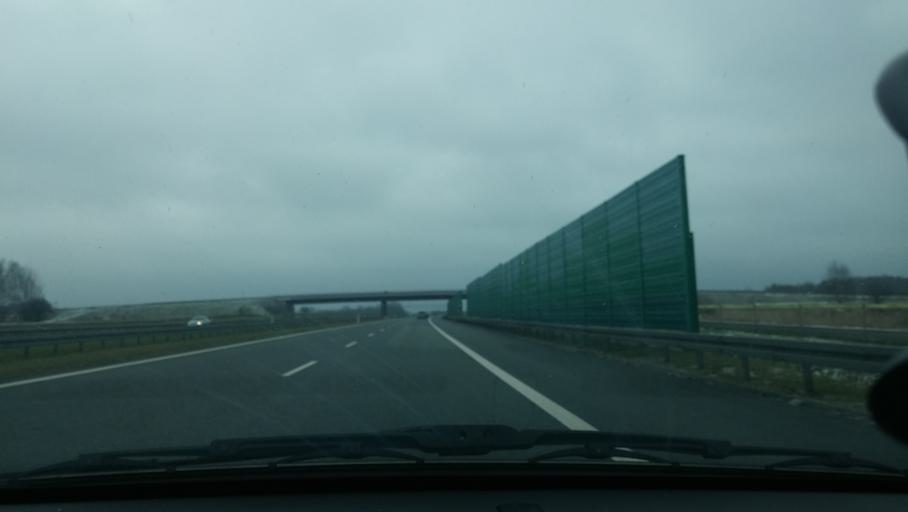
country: PL
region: Masovian Voivodeship
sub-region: Powiat minski
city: Ceglow
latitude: 52.2024
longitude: 21.7503
